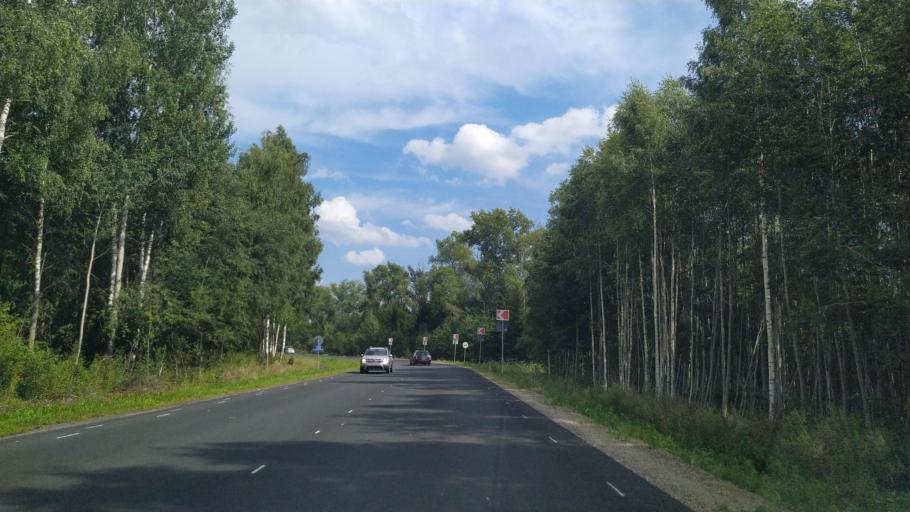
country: RU
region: Pskov
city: Pskov
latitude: 57.7078
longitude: 28.8904
